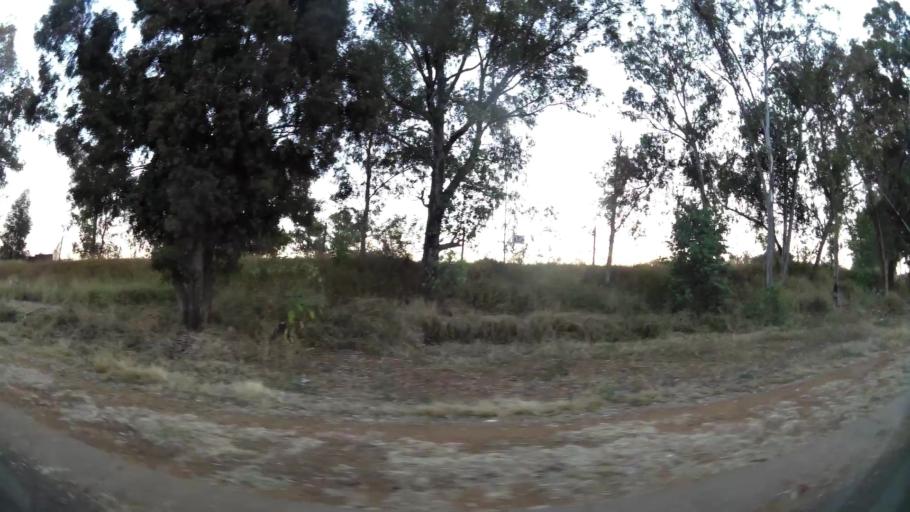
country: ZA
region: Gauteng
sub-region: City of Tshwane Metropolitan Municipality
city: Pretoria
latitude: -25.7417
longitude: 28.1506
